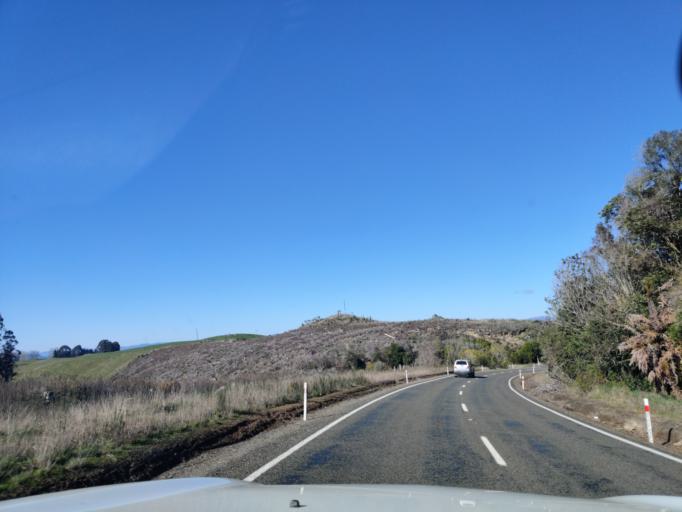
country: NZ
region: Waikato
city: Turangi
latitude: -38.7612
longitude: 175.6852
